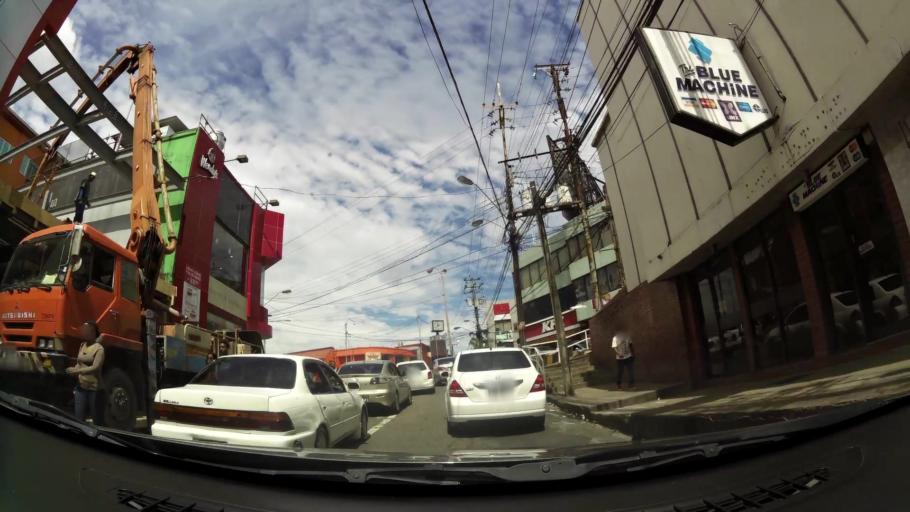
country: TT
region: City of San Fernando
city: San Fernando
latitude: 10.2796
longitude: -61.4626
